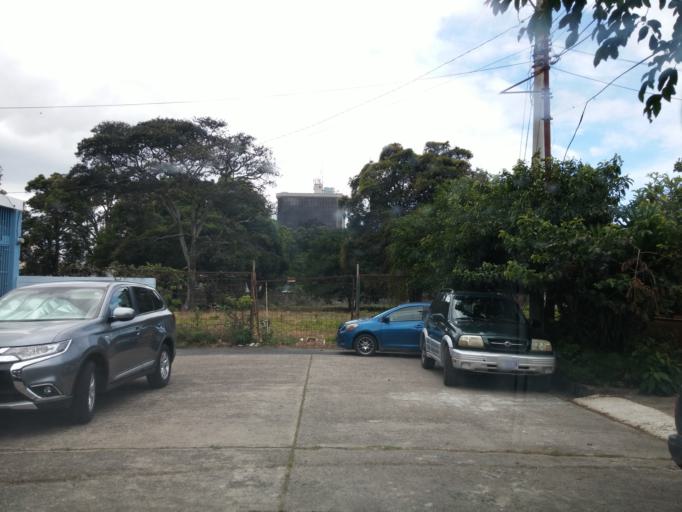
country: CR
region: San Jose
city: San Jose
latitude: 9.9393
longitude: -84.1049
